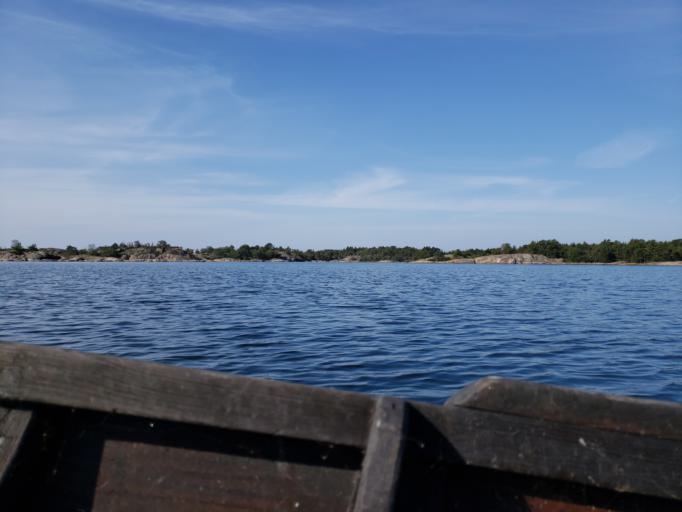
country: FI
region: Varsinais-Suomi
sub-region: Aboland-Turunmaa
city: Dragsfjaerd
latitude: 59.8554
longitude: 22.2123
